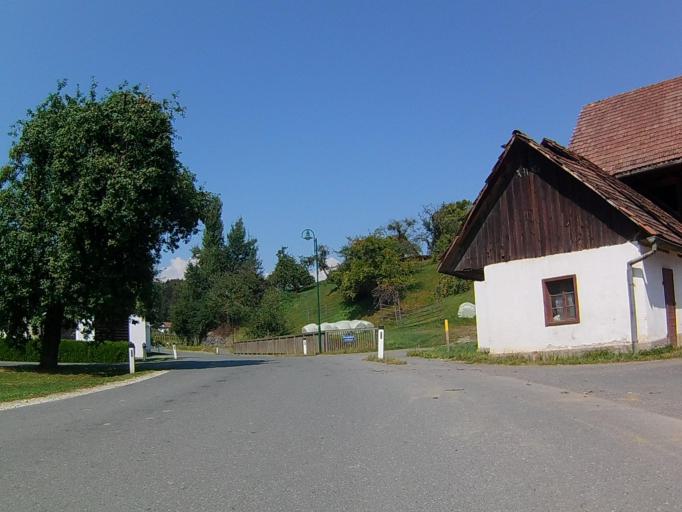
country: AT
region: Styria
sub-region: Politischer Bezirk Deutschlandsberg
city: Pitschgau
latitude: 46.7029
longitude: 15.2850
